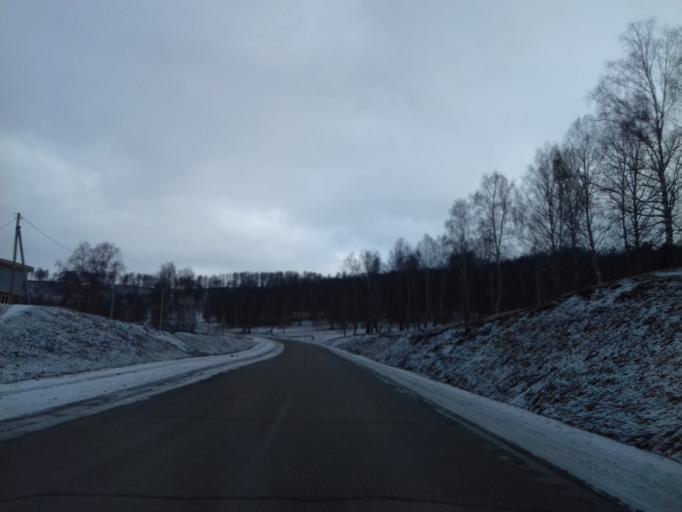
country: RU
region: Bashkortostan
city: Starosubkhangulovo
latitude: 53.2902
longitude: 57.5604
